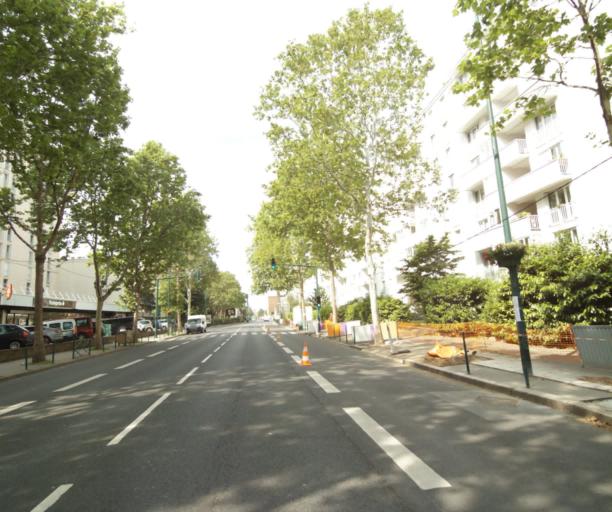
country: FR
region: Ile-de-France
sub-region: Departement des Hauts-de-Seine
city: Colombes
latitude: 48.9221
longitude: 2.2469
